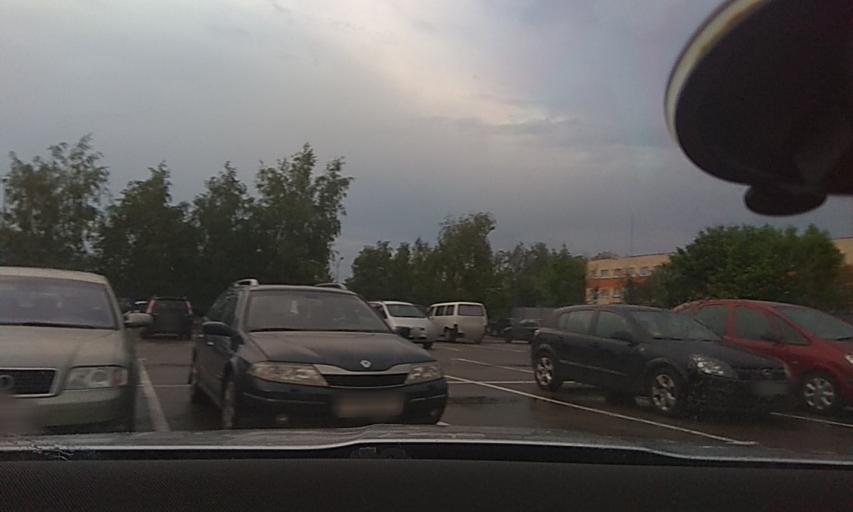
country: BY
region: Grodnenskaya
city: Hrodna
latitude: 53.6783
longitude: 23.8956
